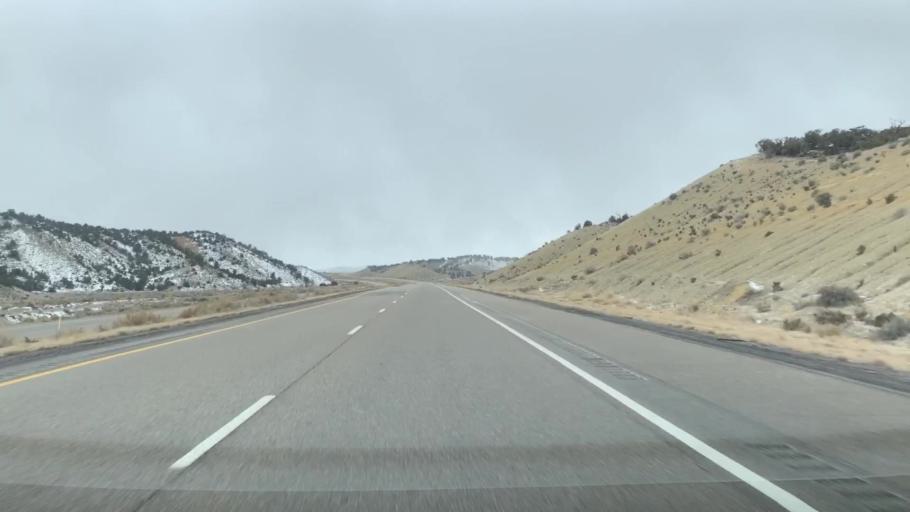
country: US
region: Utah
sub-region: Emery County
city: Ferron
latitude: 38.7931
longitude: -111.2926
